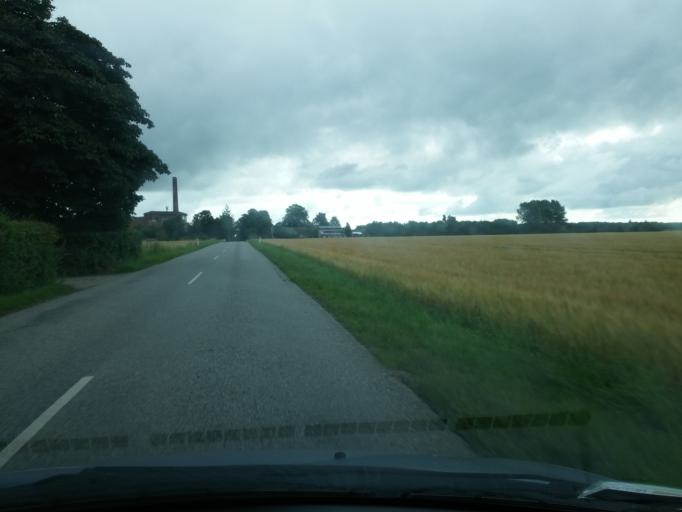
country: DK
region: South Denmark
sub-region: Odense Kommune
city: Bullerup
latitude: 55.4031
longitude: 10.5250
